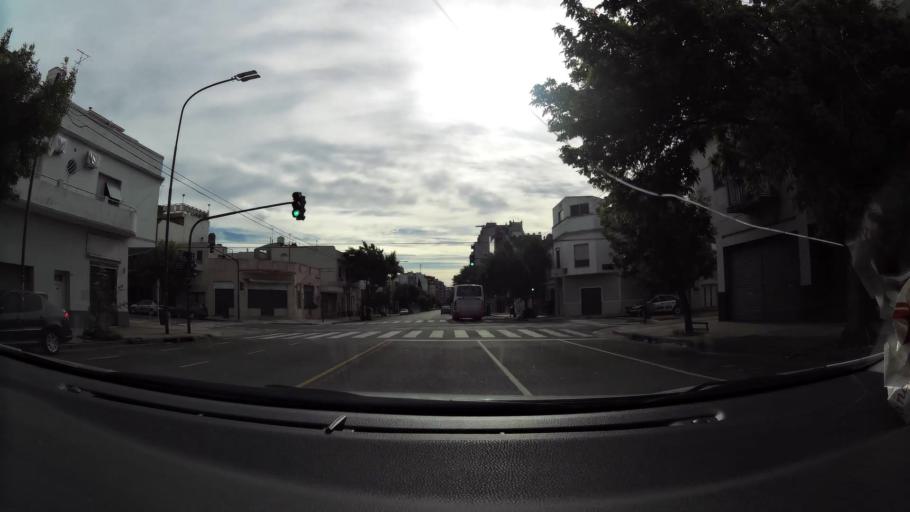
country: AR
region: Buenos Aires F.D.
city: Buenos Aires
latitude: -34.6309
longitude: -58.4216
